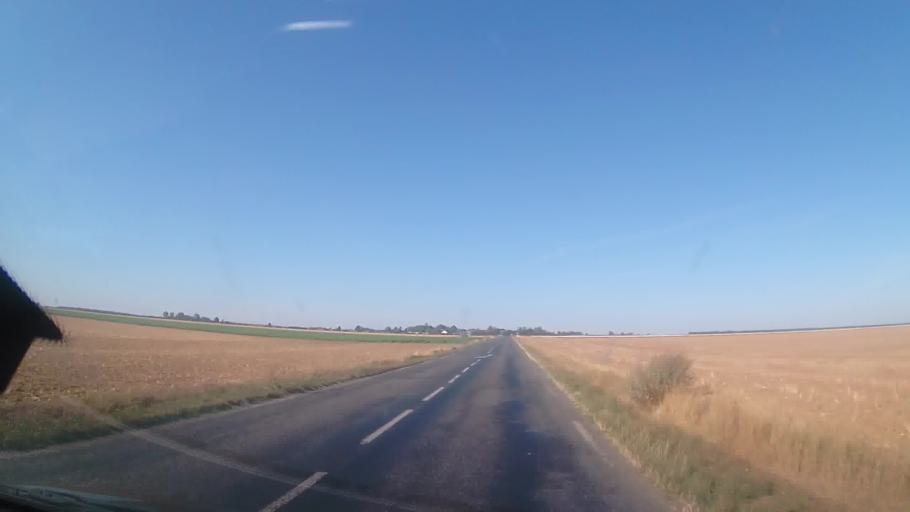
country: FR
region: Ile-de-France
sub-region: Departement de l'Essonne
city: Corbreuse
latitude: 48.4593
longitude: 1.9296
